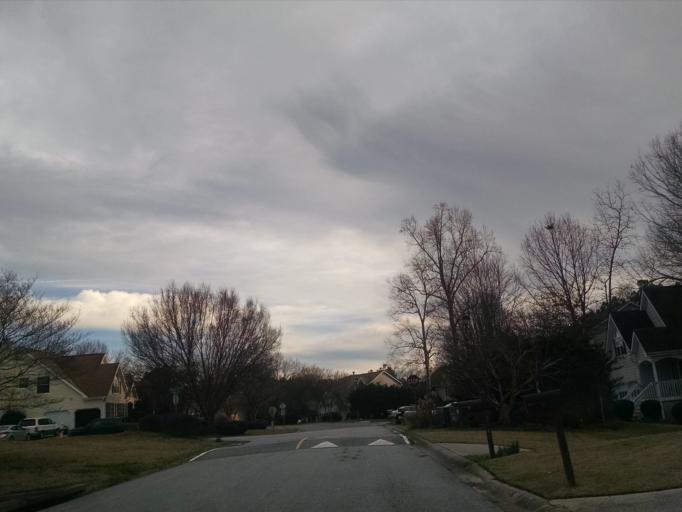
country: US
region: Georgia
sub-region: Gwinnett County
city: Sugar Hill
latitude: 34.1067
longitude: -84.0532
